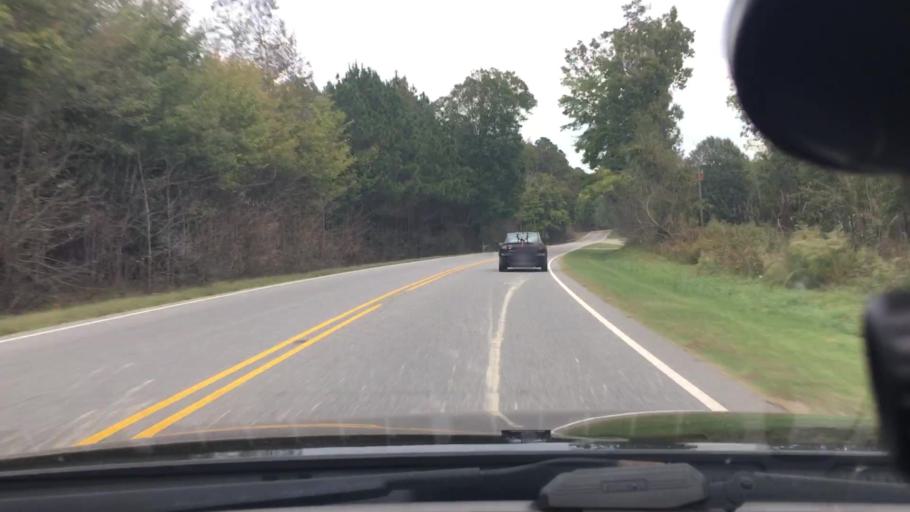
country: US
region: North Carolina
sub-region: Moore County
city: Robbins
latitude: 35.3894
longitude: -79.6478
